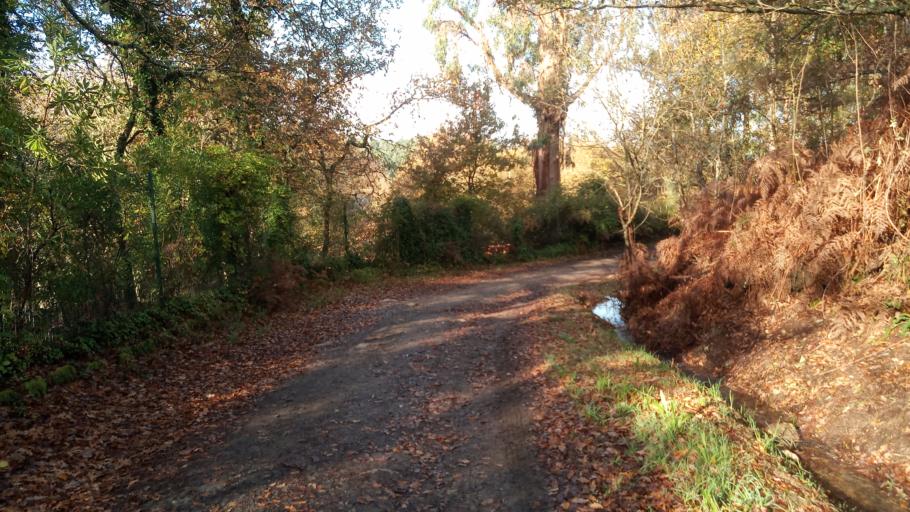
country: PT
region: Viana do Castelo
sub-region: Paredes de Coura
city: Paredes de Coura
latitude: 41.8953
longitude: -8.6140
